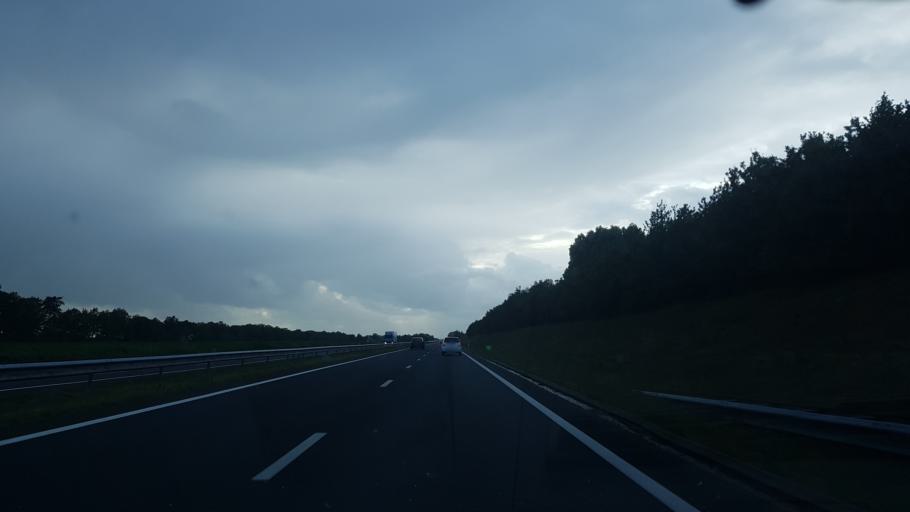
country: NL
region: Friesland
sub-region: Gemeente Smallingerland
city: Oudega
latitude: 53.1461
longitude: 5.9920
